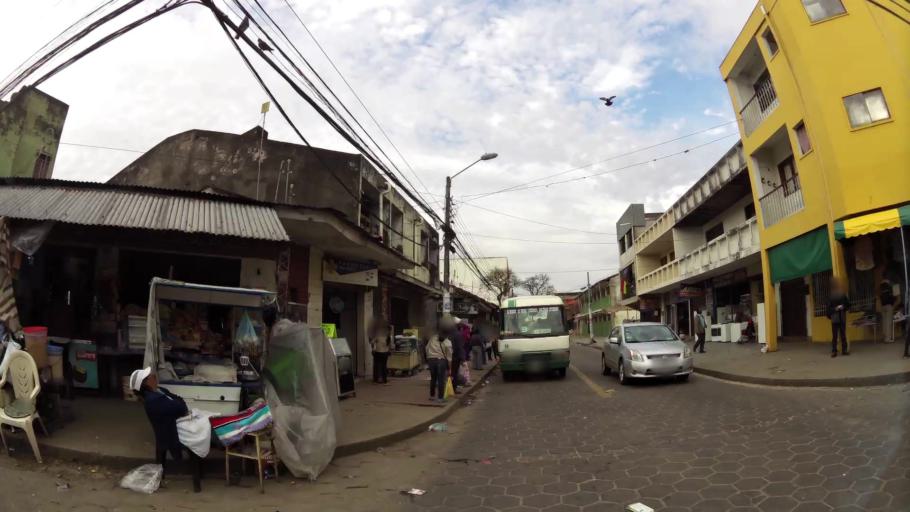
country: BO
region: Santa Cruz
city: Santa Cruz de la Sierra
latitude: -17.7801
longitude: -63.1768
